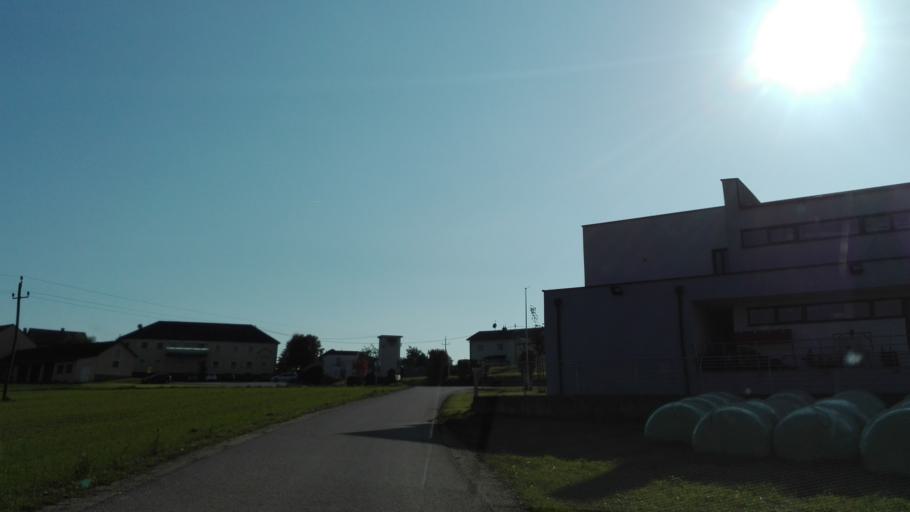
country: AT
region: Upper Austria
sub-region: Politischer Bezirk Perg
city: Perg
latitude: 48.2874
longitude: 14.5936
